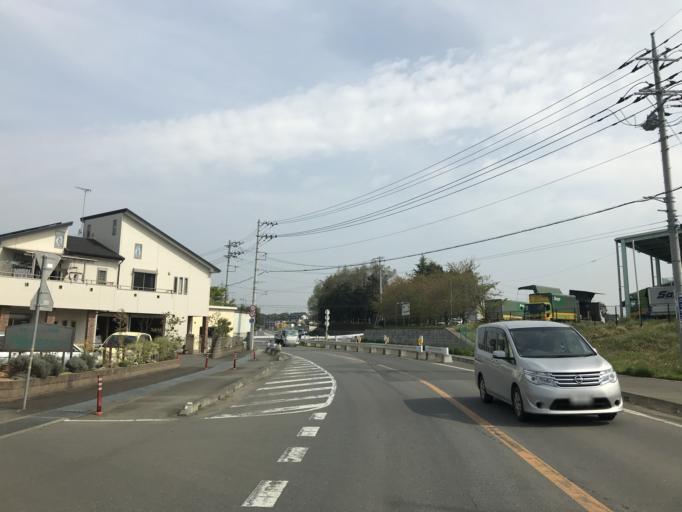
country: JP
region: Ibaraki
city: Moriya
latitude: 35.9682
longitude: 139.9903
